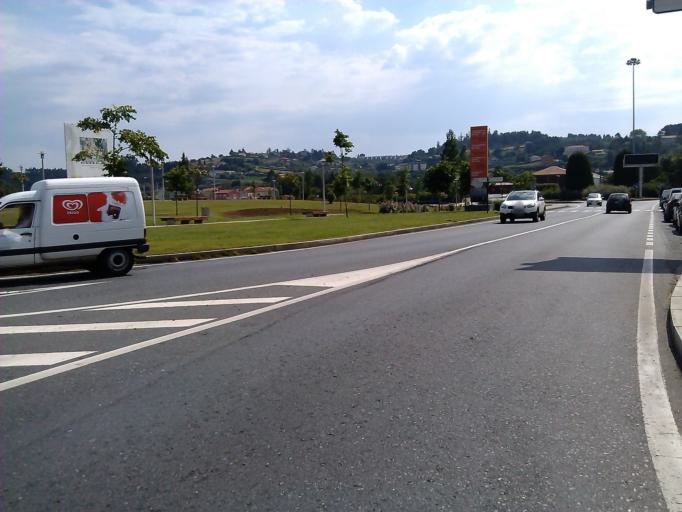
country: ES
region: Galicia
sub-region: Provincia da Coruna
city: Santiago de Compostela
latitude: 42.8864
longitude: -8.5128
